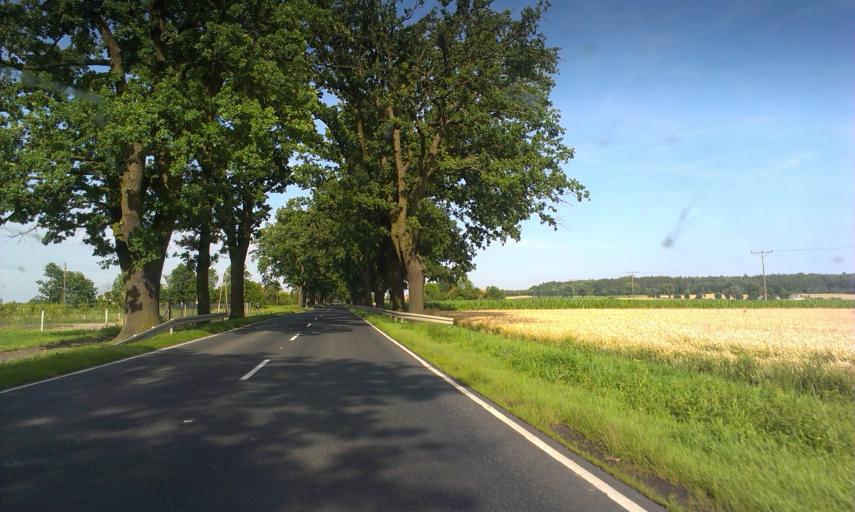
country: PL
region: Greater Poland Voivodeship
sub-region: Powiat pilski
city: Bialosliwie
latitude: 53.1549
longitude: 17.1643
